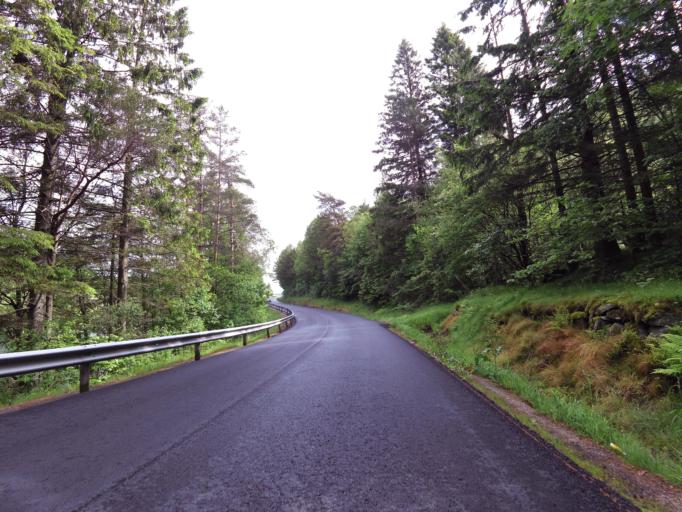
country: NO
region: Vest-Agder
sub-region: Lindesnes
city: Vigeland
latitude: 58.0580
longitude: 7.2193
